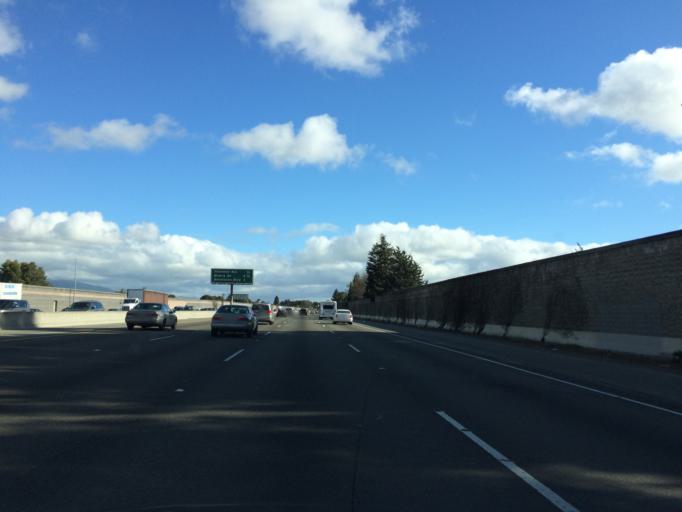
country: US
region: California
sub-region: Alameda County
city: Newark
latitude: 37.5573
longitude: -122.0320
